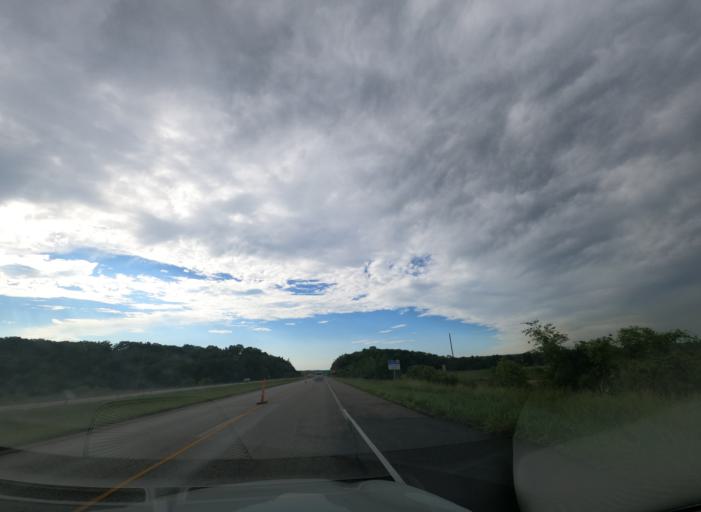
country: US
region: Missouri
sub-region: Sainte Genevieve County
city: Sainte Genevieve
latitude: 37.9953
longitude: -90.2096
